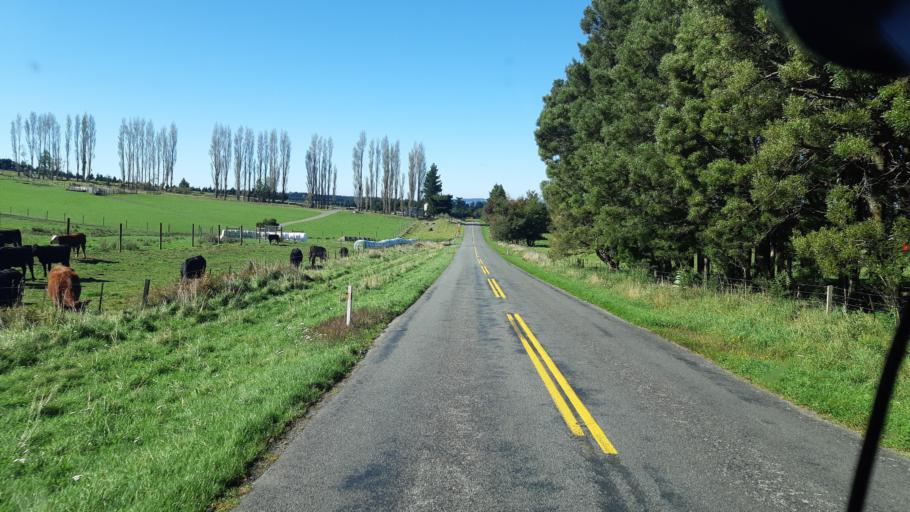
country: NZ
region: Canterbury
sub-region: Waimakariri District
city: Oxford
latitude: -43.2289
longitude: 172.2446
